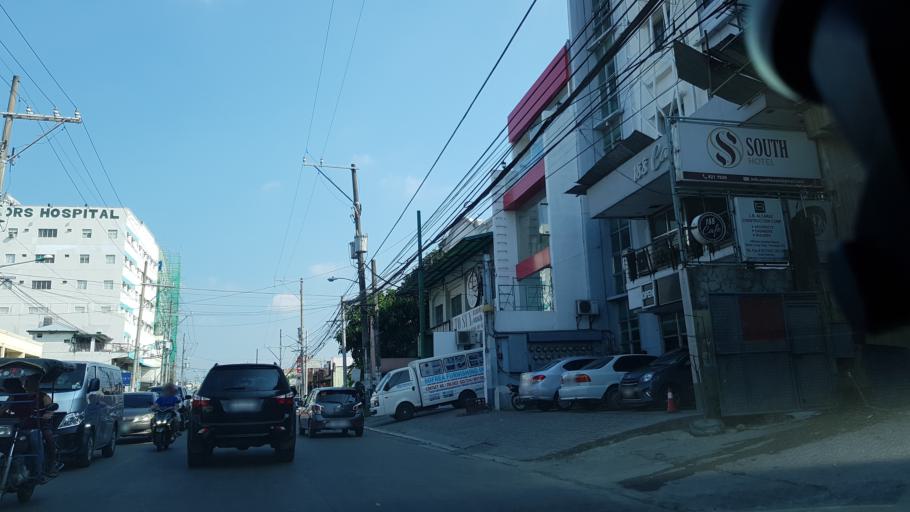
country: PH
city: Sambayanihan People's Village
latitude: 14.4865
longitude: 121.0275
